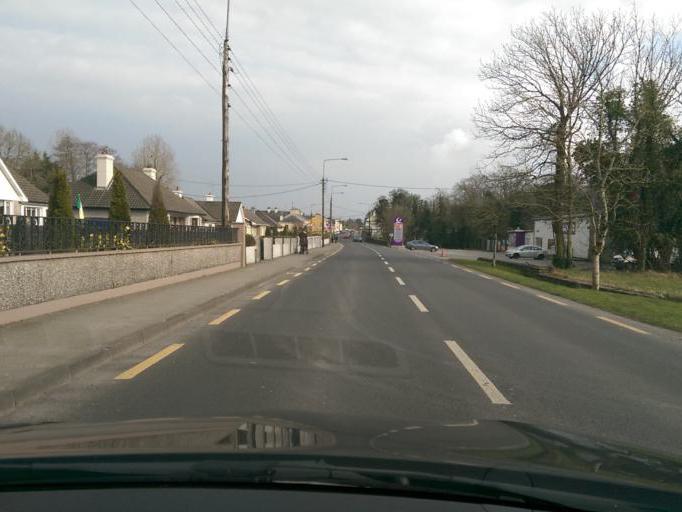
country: IE
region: Connaught
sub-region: County Galway
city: Loughrea
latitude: 53.4707
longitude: -8.5040
